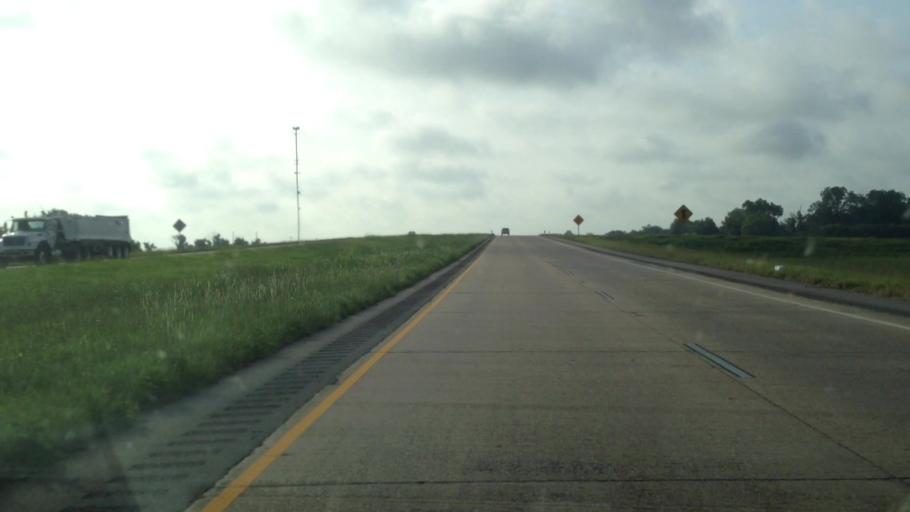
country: US
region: Louisiana
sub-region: Rapides Parish
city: Lecompte
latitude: 31.0158
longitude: -92.3794
